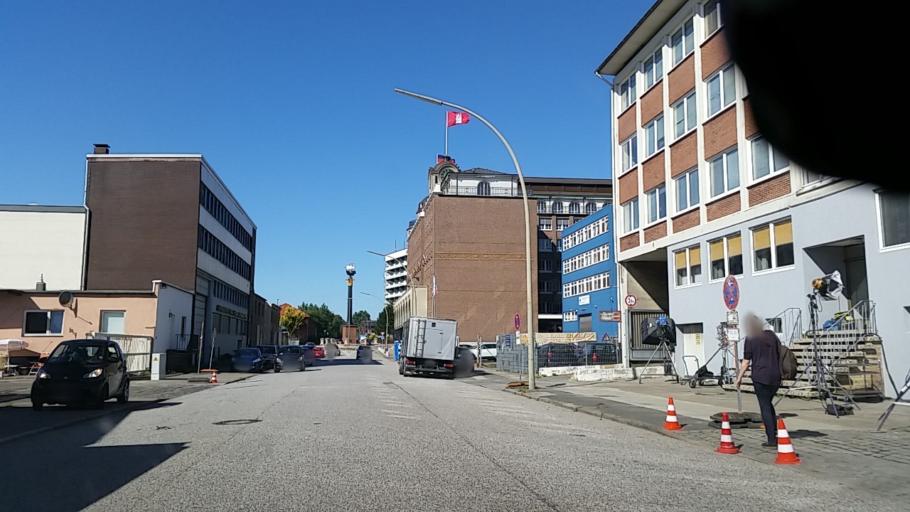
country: DE
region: Hamburg
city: Rothenburgsort
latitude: 53.5464
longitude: 10.0497
